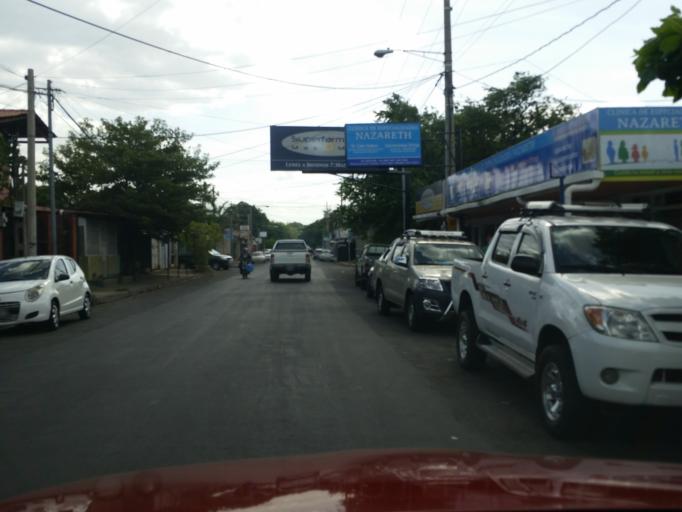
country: NI
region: Managua
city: Managua
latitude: 12.1420
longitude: -86.2634
